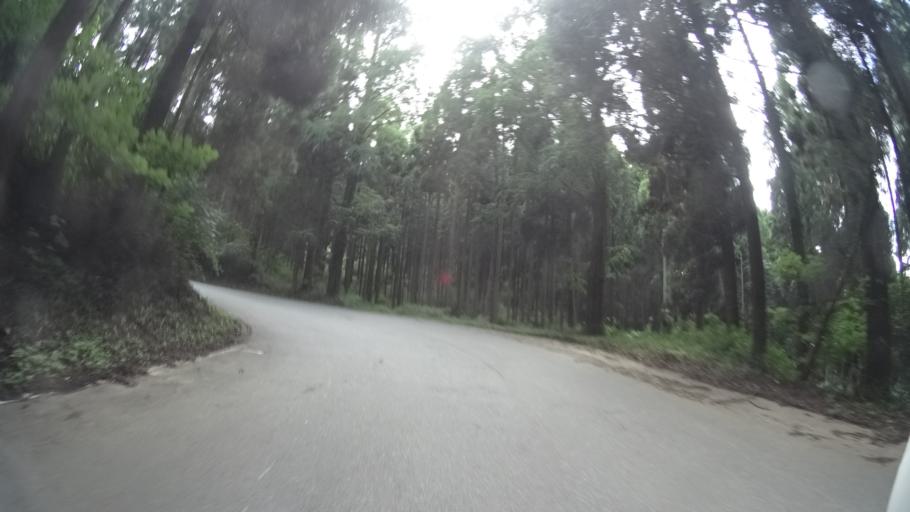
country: JP
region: Kumamoto
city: Aso
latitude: 32.8101
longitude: 131.1331
